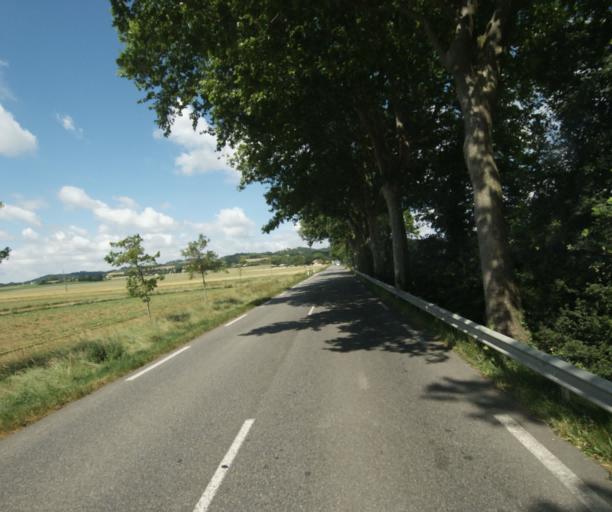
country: FR
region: Midi-Pyrenees
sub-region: Departement de la Haute-Garonne
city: Saint-Felix-Lauragais
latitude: 43.4481
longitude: 1.9240
